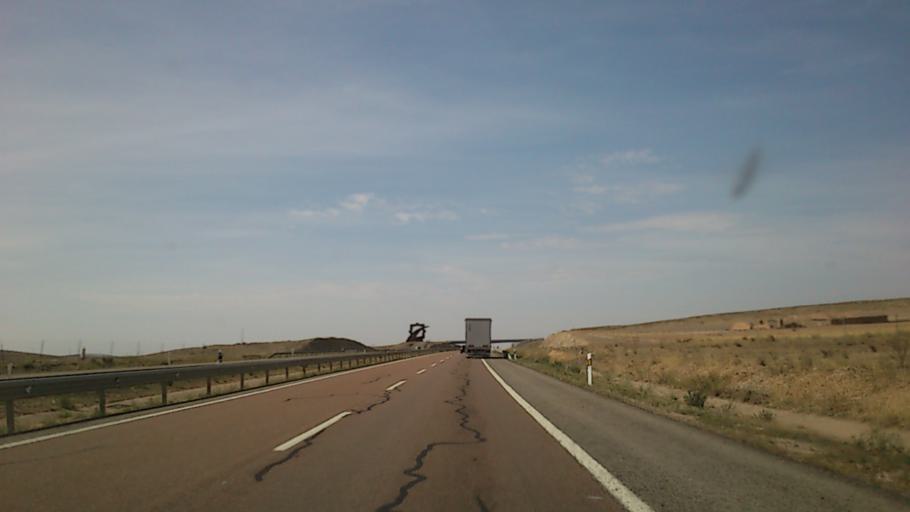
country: ES
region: Aragon
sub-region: Provincia de Teruel
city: Singra
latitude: 40.6353
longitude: -1.3102
